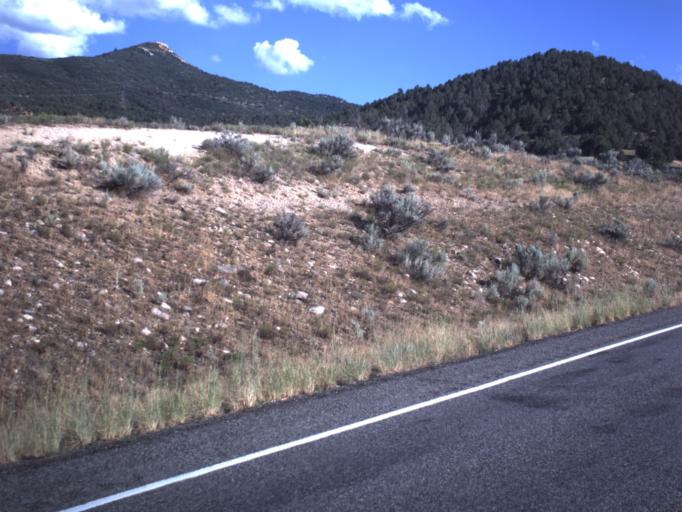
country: US
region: Utah
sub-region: Utah County
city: Woodland Hills
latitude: 39.9436
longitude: -111.5404
